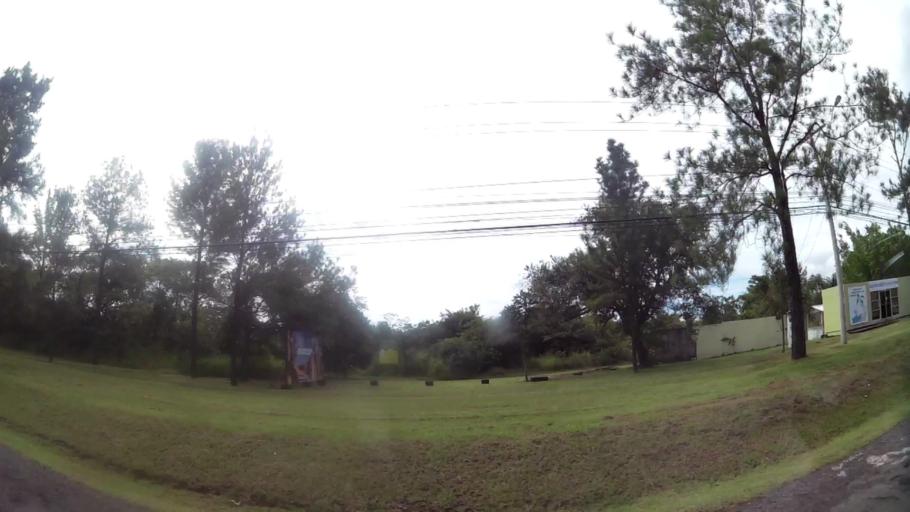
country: PA
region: Panama
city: Nueva Gorgona
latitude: 8.5366
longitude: -79.9007
